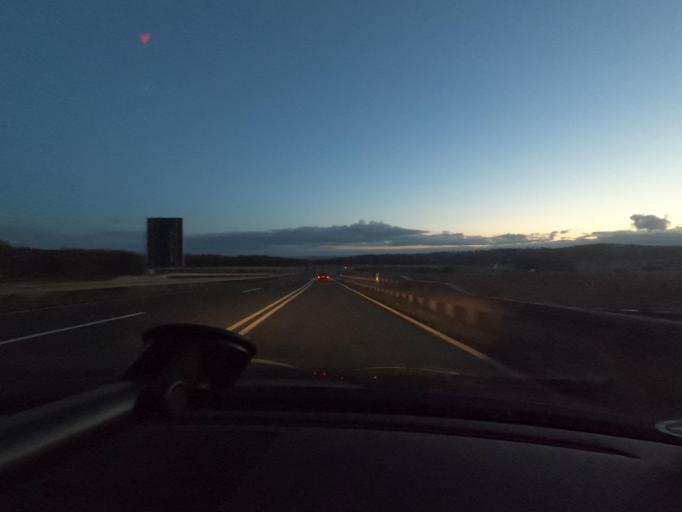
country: DE
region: Lower Saxony
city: Bad Sachsa
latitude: 51.5784
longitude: 10.5148
